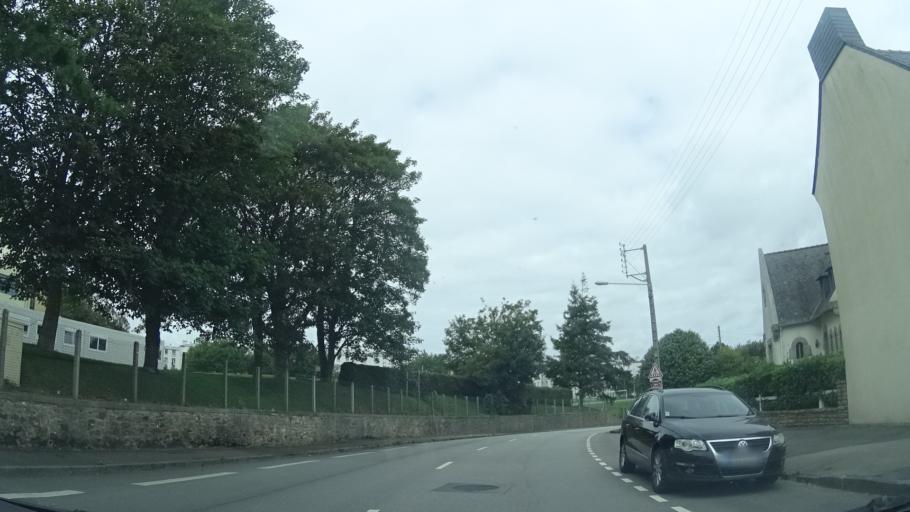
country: FR
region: Brittany
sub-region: Departement du Finistere
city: Brest
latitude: 48.4036
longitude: -4.4578
